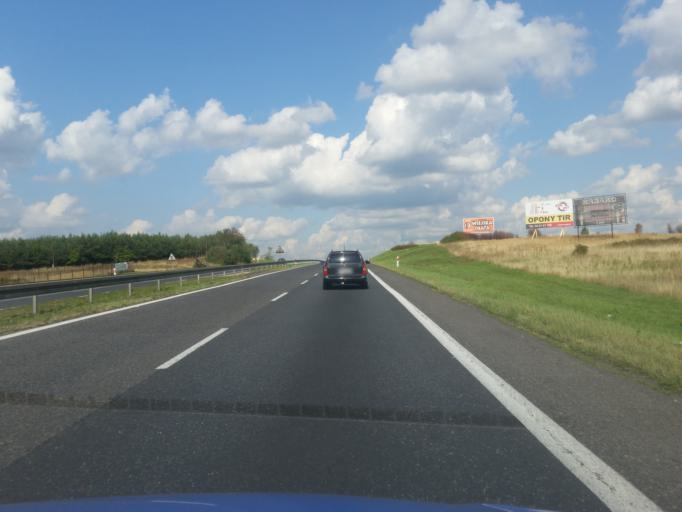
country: PL
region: Silesian Voivodeship
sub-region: Powiat myszkowski
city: Kozieglowy
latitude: 50.5795
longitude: 19.1635
